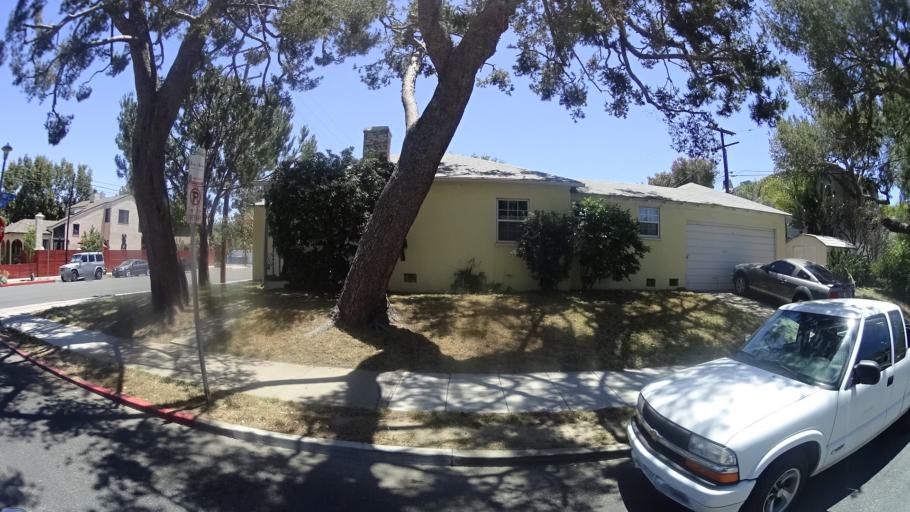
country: US
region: California
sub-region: Los Angeles County
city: Santa Monica
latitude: 34.0101
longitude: -118.4627
